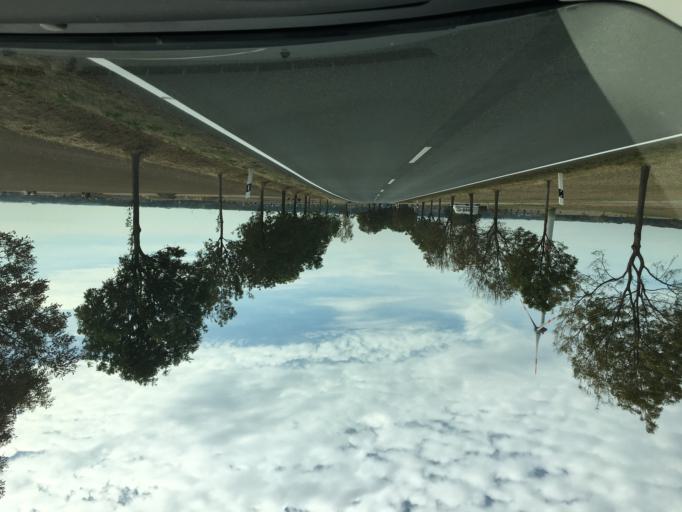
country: DE
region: Saxony
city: Stauchitz
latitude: 51.2755
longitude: 13.2086
